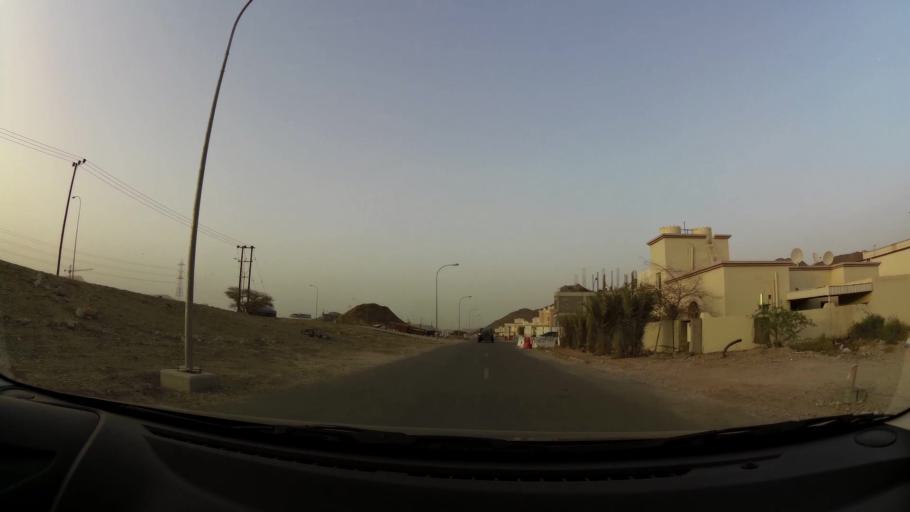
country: OM
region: Muhafazat Masqat
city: Bawshar
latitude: 23.4883
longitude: 58.3154
